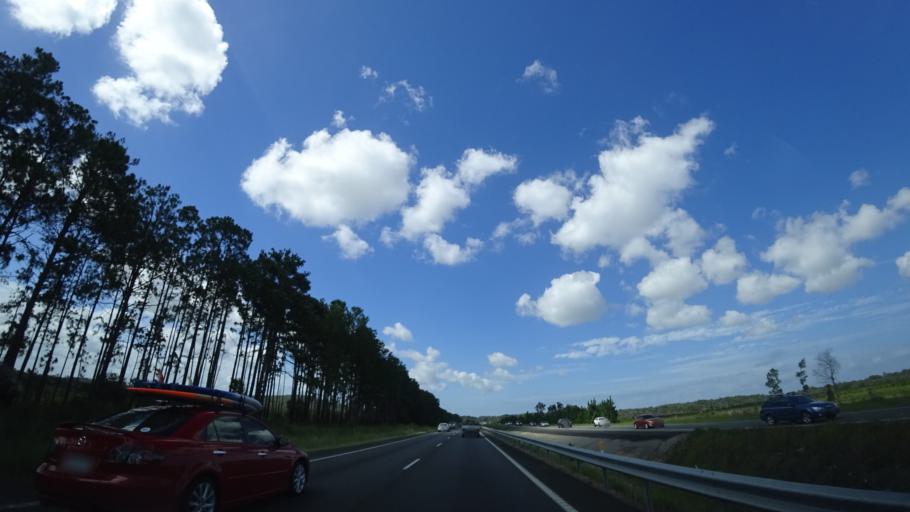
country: AU
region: Queensland
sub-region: Sunshine Coast
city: Little Mountain
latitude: -26.8126
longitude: 153.0383
